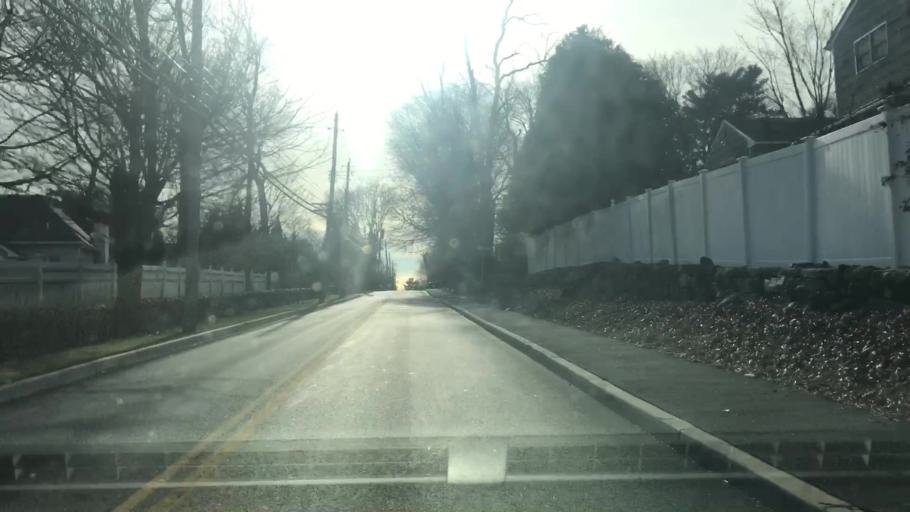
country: US
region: New York
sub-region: Westchester County
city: Greenville
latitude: 40.9931
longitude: -73.8264
